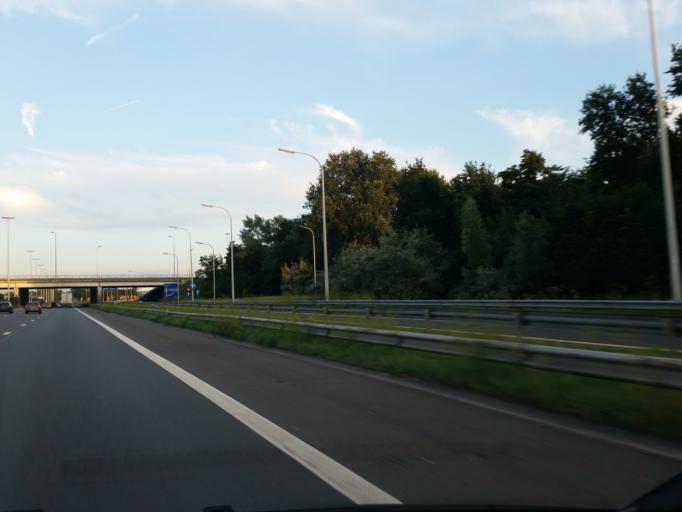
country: BE
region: Flanders
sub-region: Provincie West-Vlaanderen
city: Oostkamp
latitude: 51.1569
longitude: 3.2098
